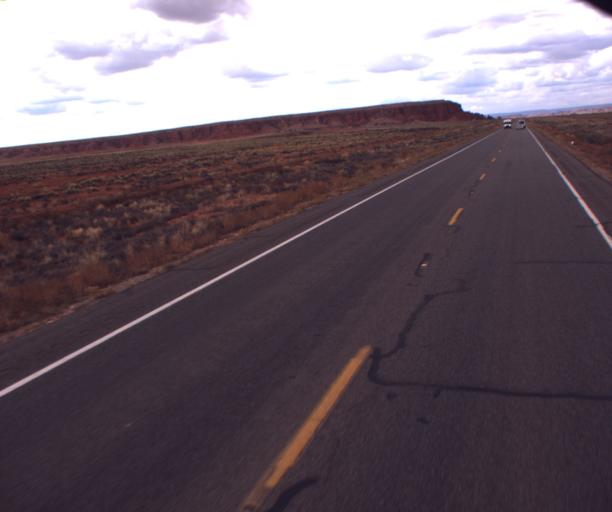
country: US
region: Arizona
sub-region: Navajo County
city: Kayenta
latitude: 36.7810
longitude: -109.9889
